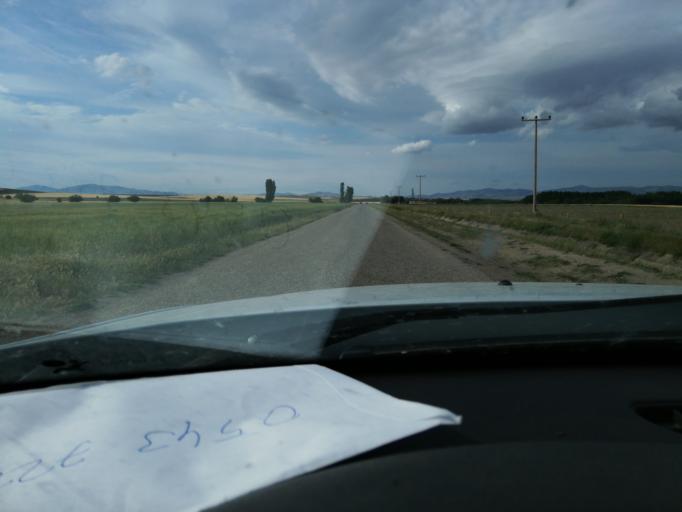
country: TR
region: Kirsehir
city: Kirsehir
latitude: 39.0047
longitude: 34.1196
